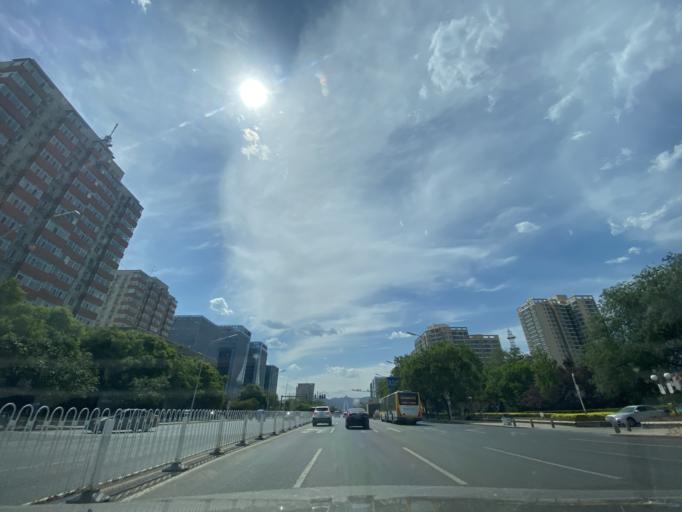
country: CN
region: Beijing
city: Lugu
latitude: 39.9061
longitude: 116.1822
